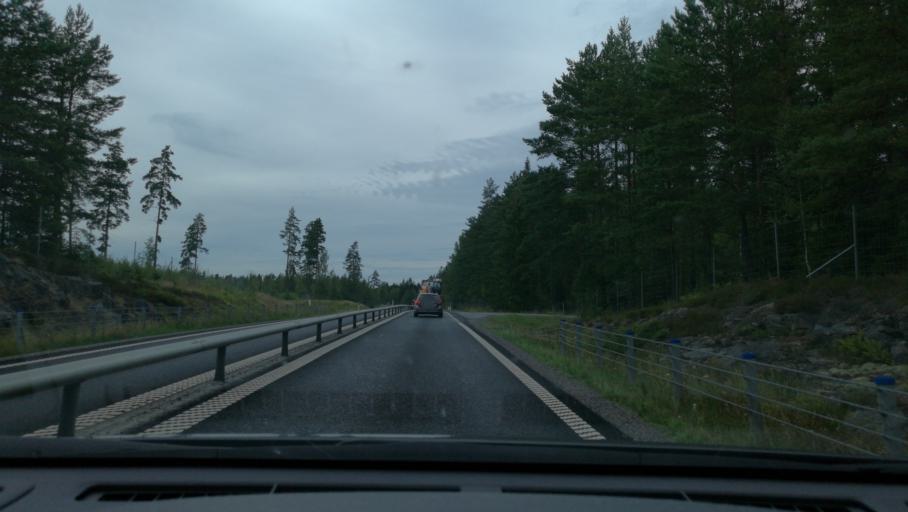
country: SE
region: Soedermanland
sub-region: Katrineholms Kommun
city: Katrineholm
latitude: 58.8950
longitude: 16.2094
